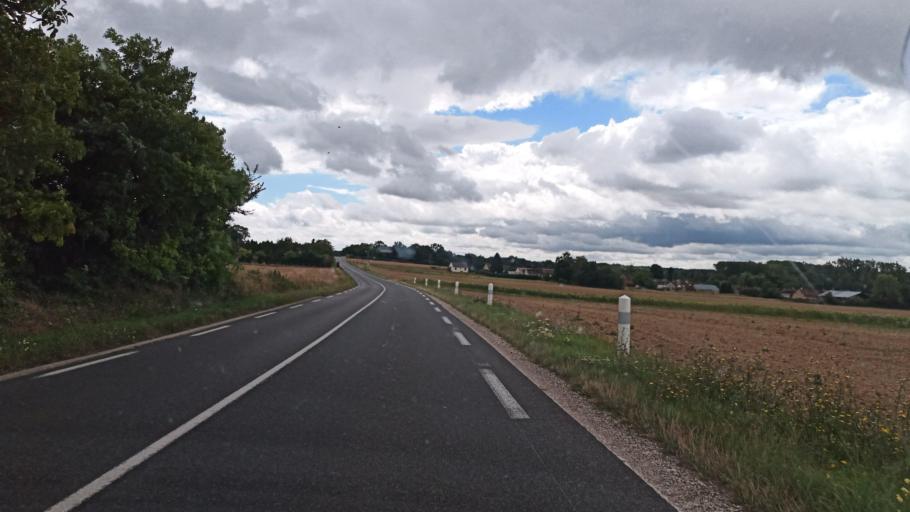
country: FR
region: Ile-de-France
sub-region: Departement de Seine-et-Marne
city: Voulx
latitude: 48.3119
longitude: 2.9475
